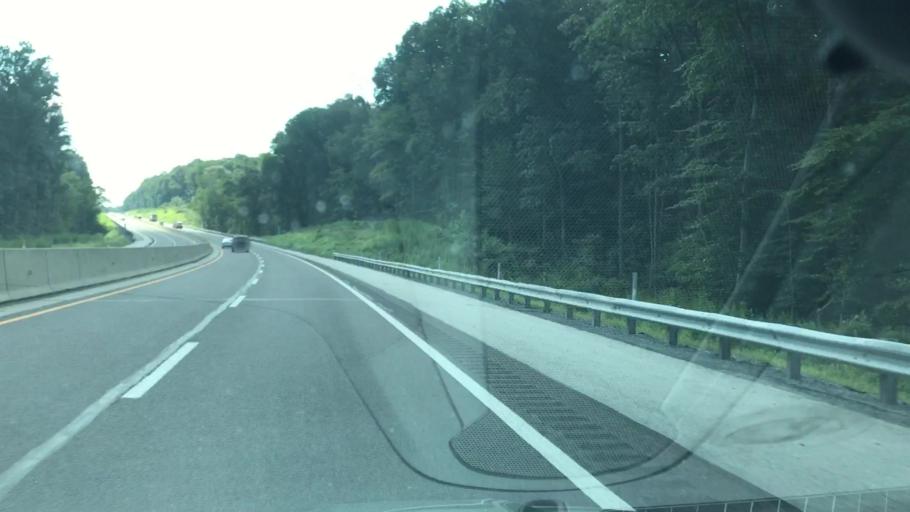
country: US
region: Pennsylvania
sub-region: Lebanon County
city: Cornwall
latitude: 40.2280
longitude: -76.4902
